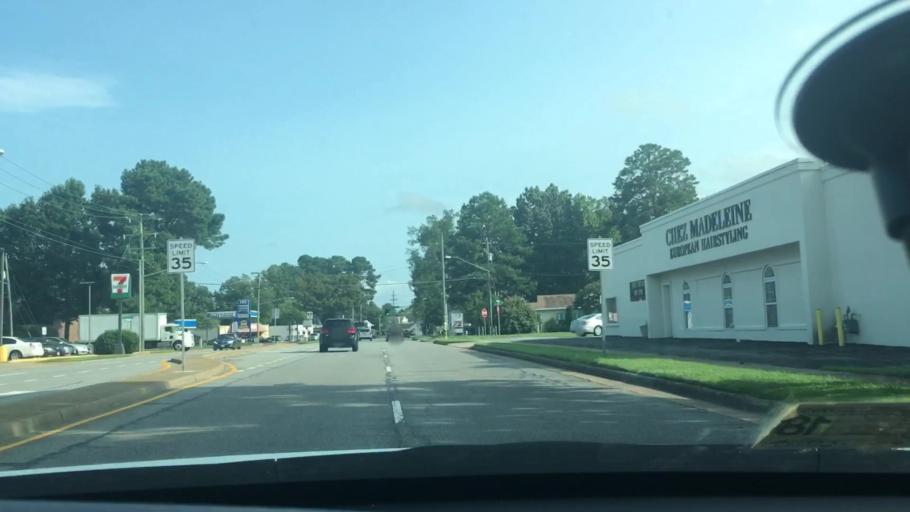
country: US
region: Virginia
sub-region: City of Virginia Beach
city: Virginia Beach
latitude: 36.8540
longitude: -75.9954
